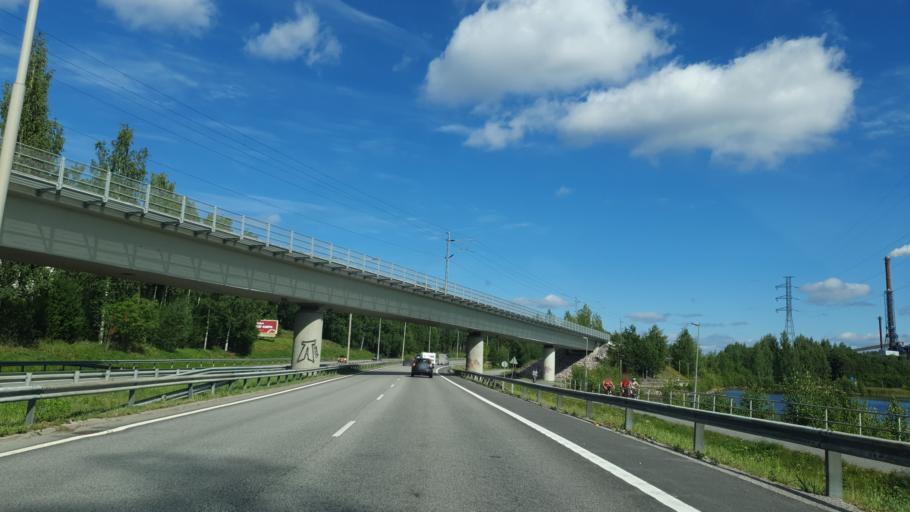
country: FI
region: Central Finland
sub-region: Jyvaeskylae
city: Jyvaeskylae
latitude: 62.2399
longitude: 25.7961
